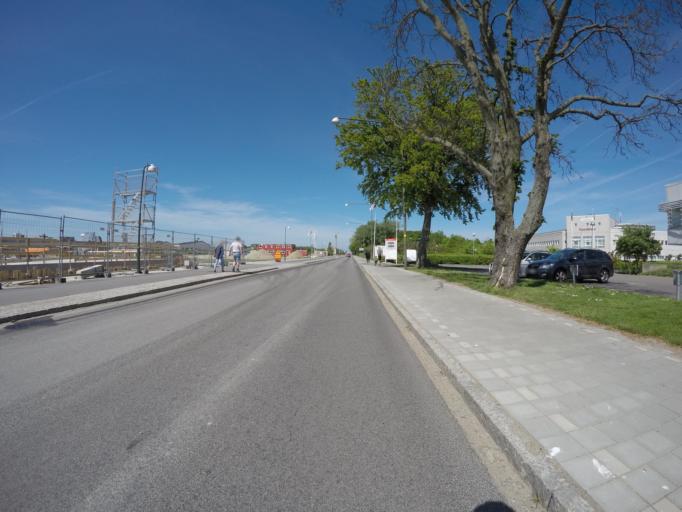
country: SE
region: Skane
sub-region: Malmo
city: Bunkeflostrand
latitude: 55.5906
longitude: 12.9408
